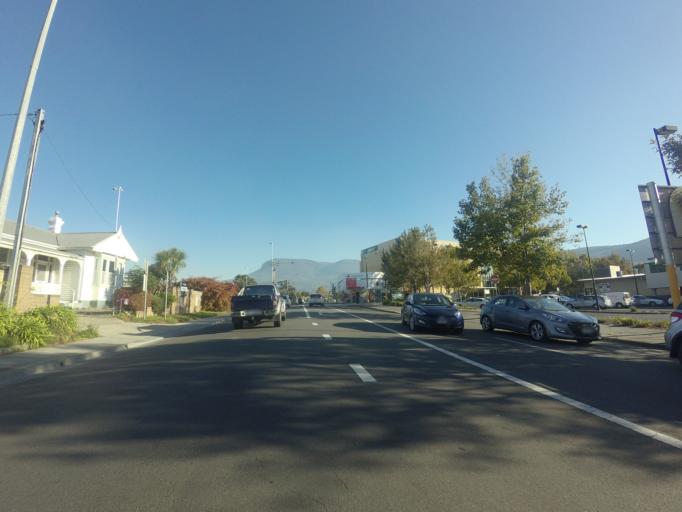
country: AU
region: Tasmania
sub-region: Glenorchy
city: Glenorchy
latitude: -42.8341
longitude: 147.2786
